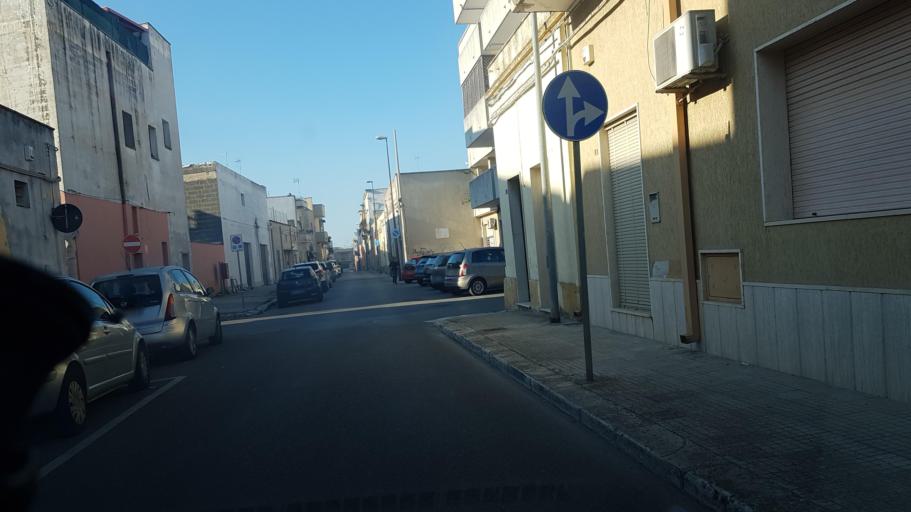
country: IT
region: Apulia
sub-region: Provincia di Brindisi
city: Mesagne
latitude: 40.5602
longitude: 17.8138
